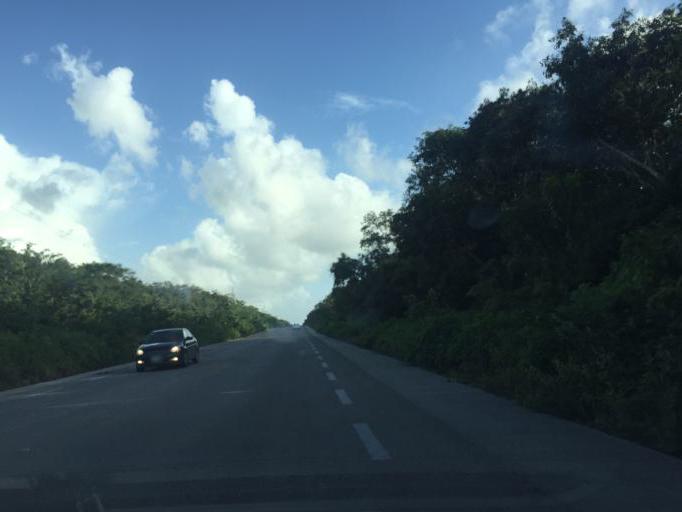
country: MX
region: Quintana Roo
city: Coba
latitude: 20.4843
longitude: -87.6983
